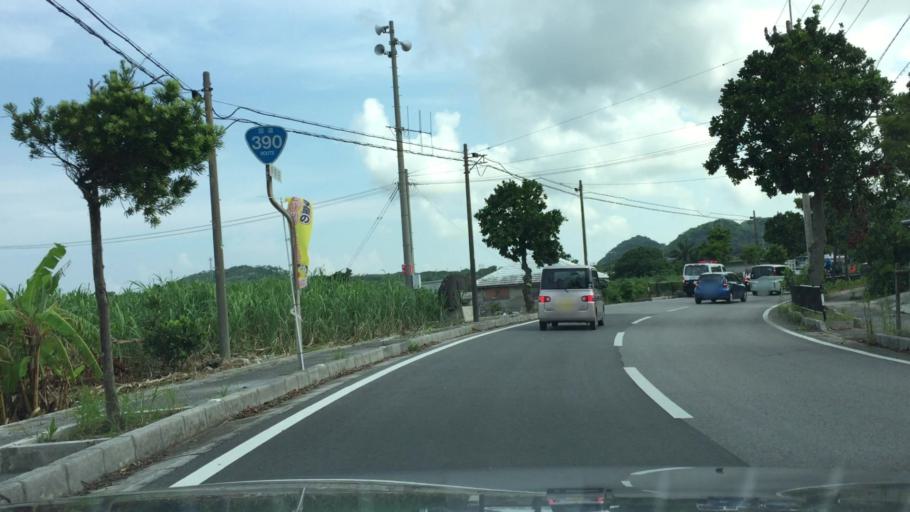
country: JP
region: Okinawa
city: Ishigaki
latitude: 24.4576
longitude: 124.2494
